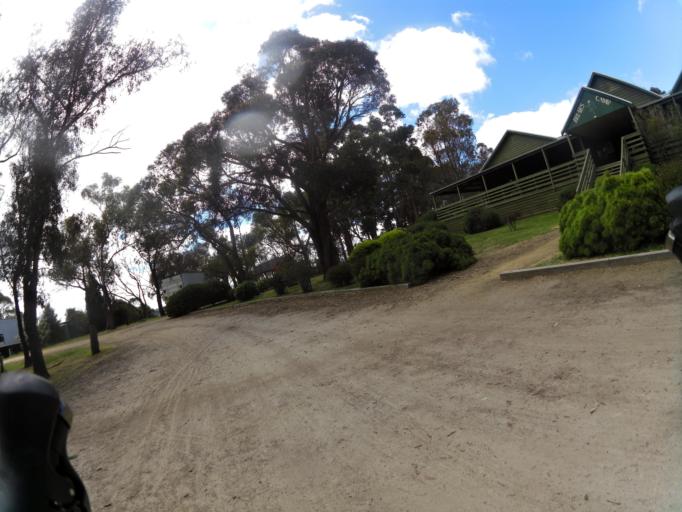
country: AU
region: Victoria
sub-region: Mornington Peninsula
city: Mount Martha
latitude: -38.2734
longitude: 145.0405
